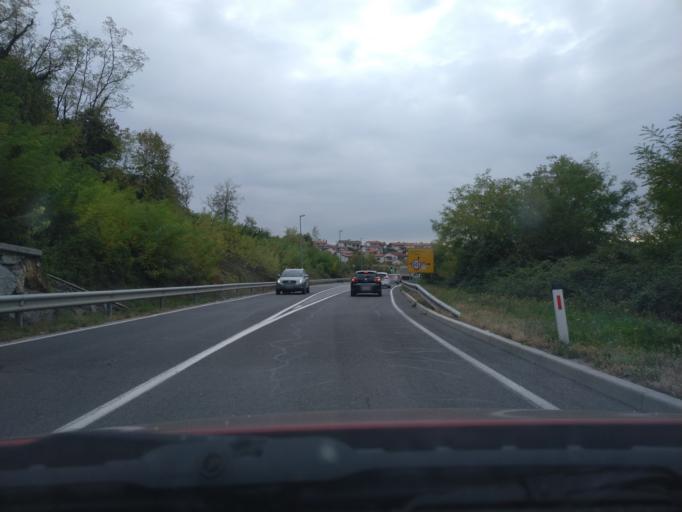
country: SI
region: Nova Gorica
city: Solkan
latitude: 45.9640
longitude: 13.6547
